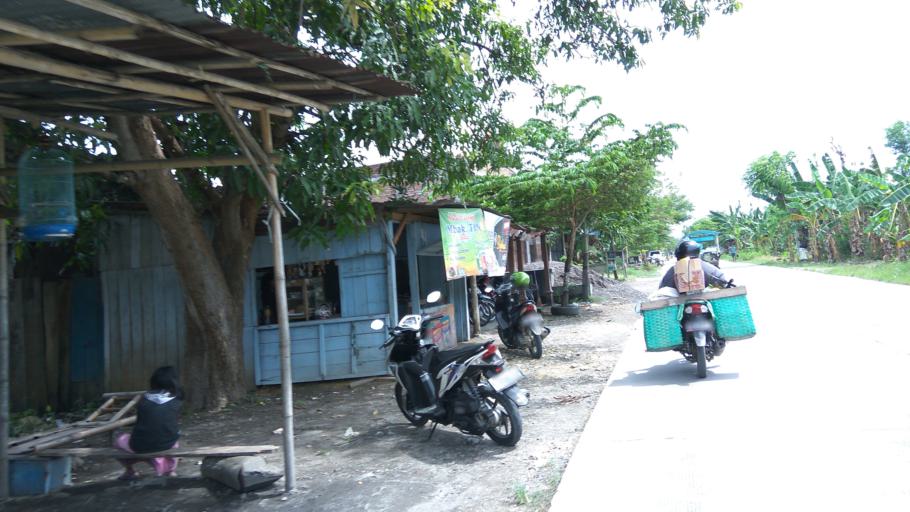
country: ID
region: Central Java
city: Mranggen
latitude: -7.0688
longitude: 110.6648
